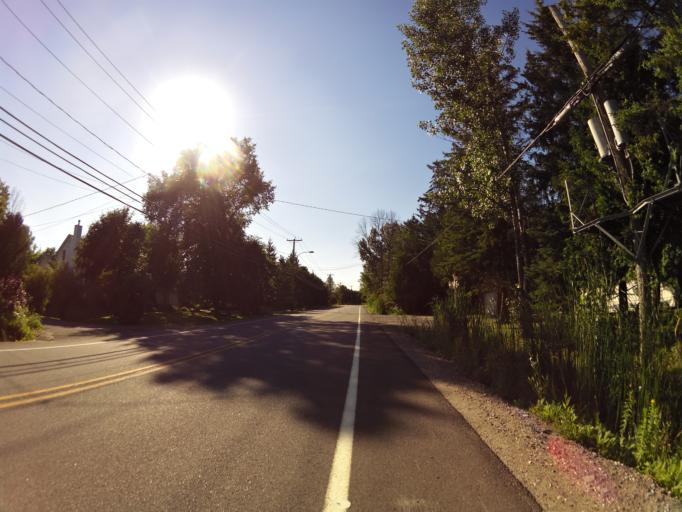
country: CA
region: Quebec
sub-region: Outaouais
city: Gatineau
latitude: 45.4958
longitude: -75.7762
